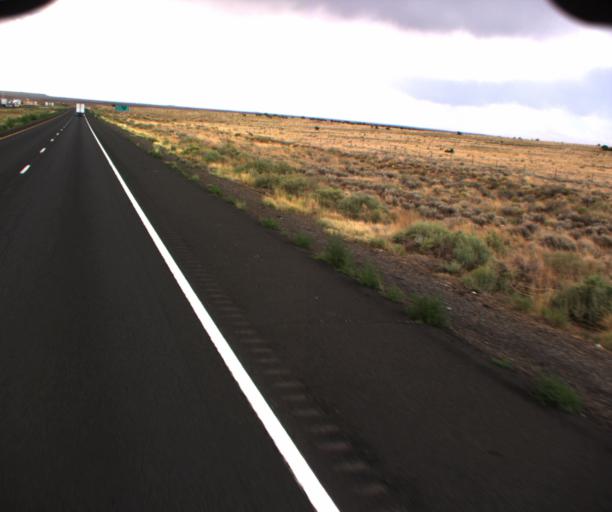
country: US
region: Arizona
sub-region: Coconino County
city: LeChee
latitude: 35.1027
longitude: -110.9922
